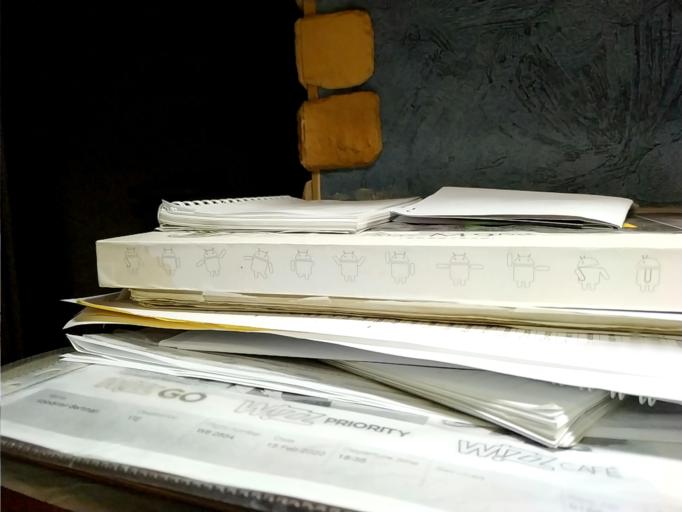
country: RU
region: Arkhangelskaya
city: Onega
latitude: 63.3190
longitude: 38.2523
